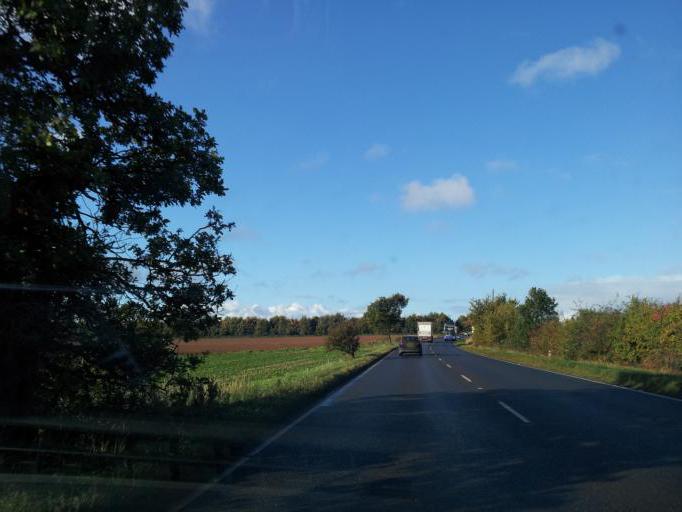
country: GB
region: England
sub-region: Norfolk
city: King's Lynn
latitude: 52.7156
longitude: 0.4829
